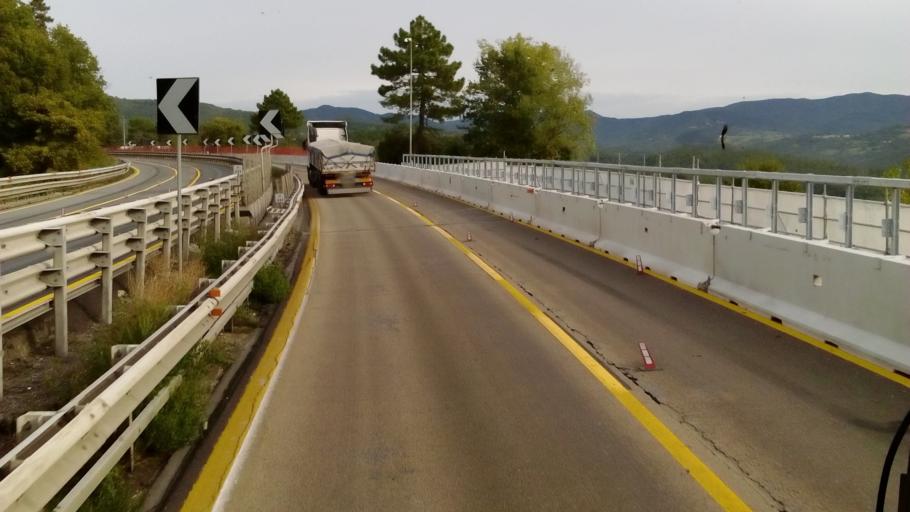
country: IT
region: Tuscany
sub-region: Province of Florence
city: Barberino di Mugello
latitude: 44.0178
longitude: 11.2245
